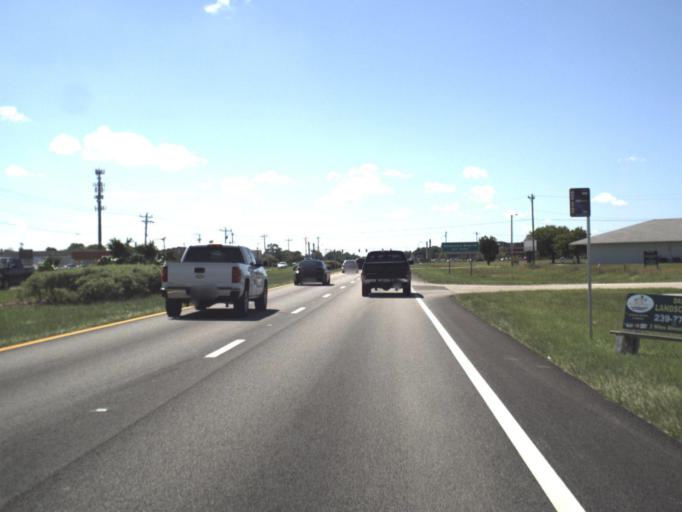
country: US
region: Florida
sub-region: Lee County
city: Lochmoor Waterway Estates
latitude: 26.6624
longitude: -81.9525
